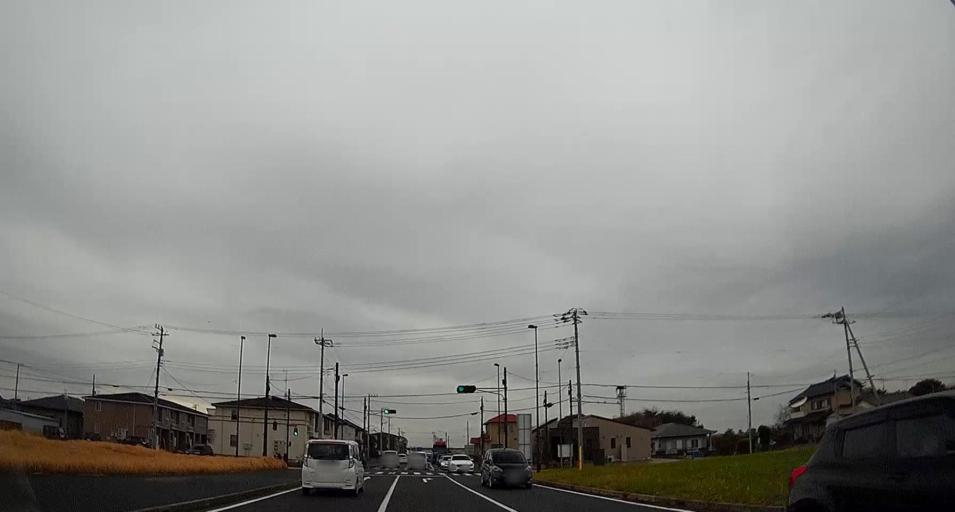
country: JP
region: Chiba
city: Kisarazu
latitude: 35.4375
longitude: 139.9270
